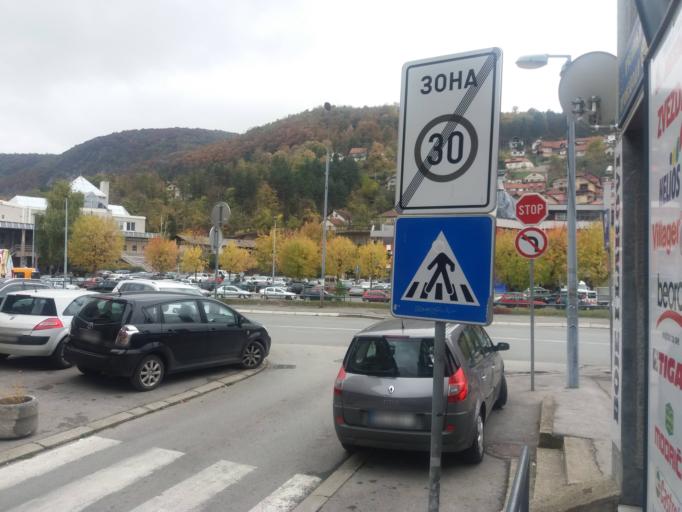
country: RS
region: Central Serbia
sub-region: Zlatiborski Okrug
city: Uzice
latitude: 43.8546
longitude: 19.8404
